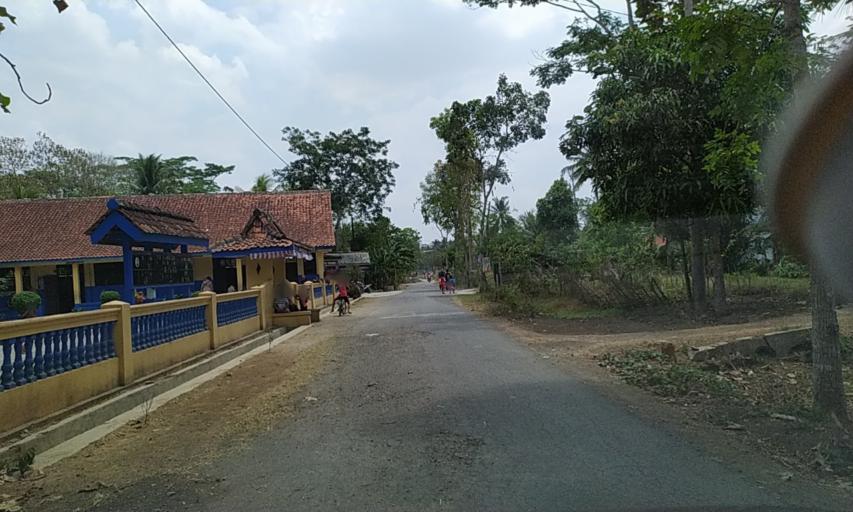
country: ID
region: Central Java
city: Cipariuk
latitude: -7.5006
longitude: 108.7699
